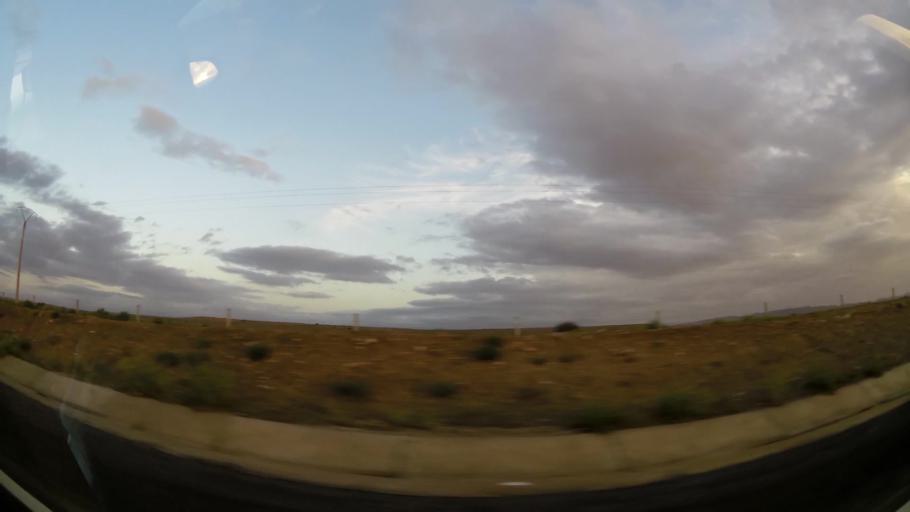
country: MA
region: Oriental
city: Taourirt
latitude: 34.5494
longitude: -2.8782
